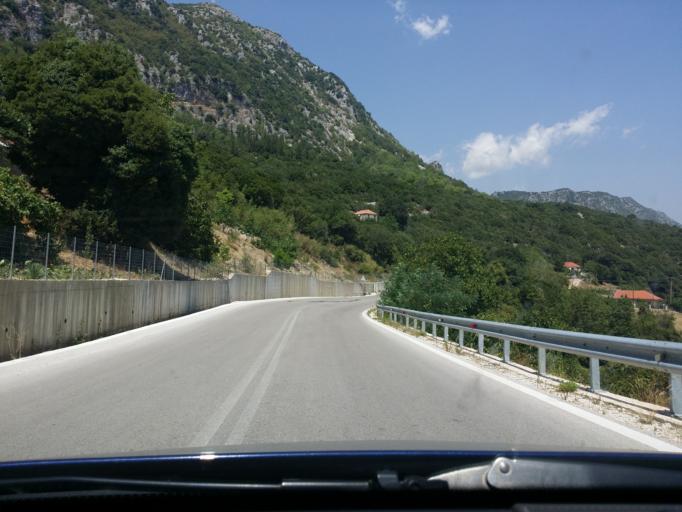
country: GR
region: Epirus
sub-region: Nomos Artas
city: Agios Dimitrios
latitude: 39.3295
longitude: 20.9994
